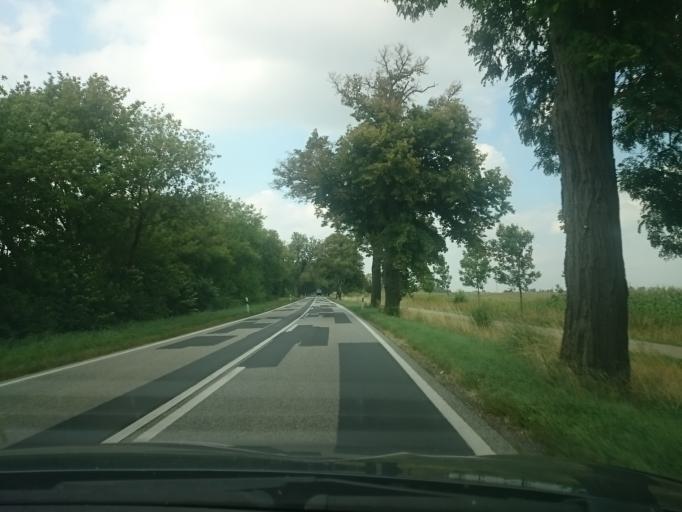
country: DE
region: Mecklenburg-Vorpommern
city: Ducherow
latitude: 53.7486
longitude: 13.7814
